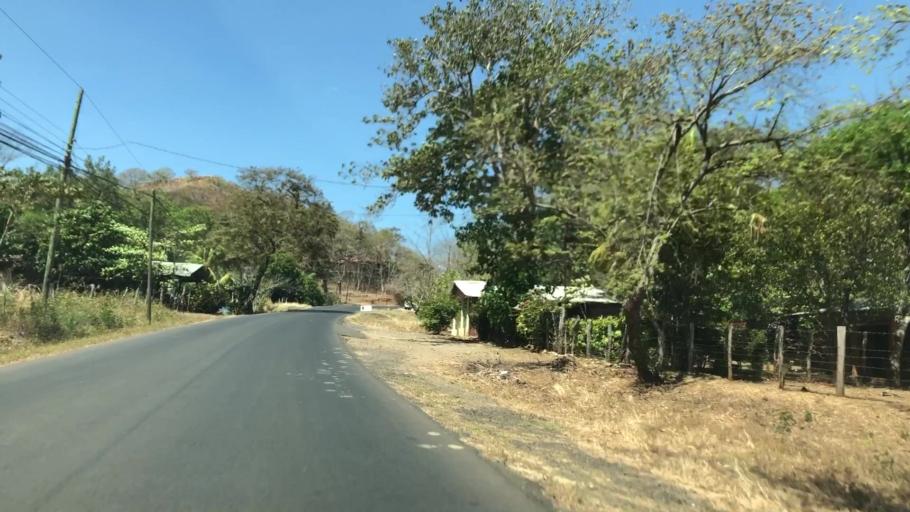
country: CR
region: Guanacaste
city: Sardinal
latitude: 10.3655
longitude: -85.7962
